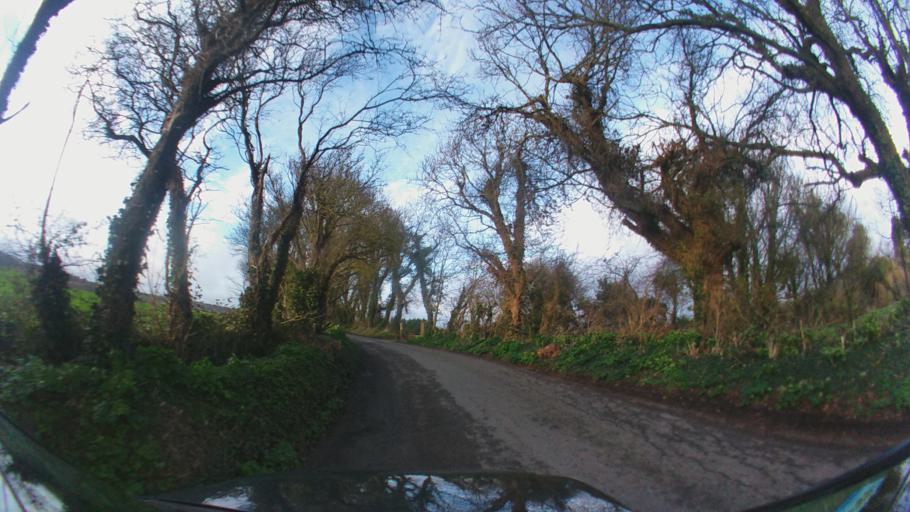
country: IE
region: Leinster
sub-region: Fingal County
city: Skerries
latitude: 53.5718
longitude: -6.1322
